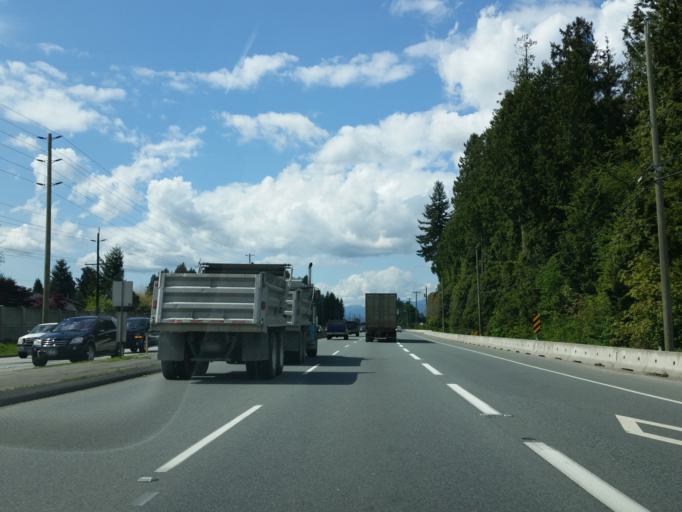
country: CA
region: British Columbia
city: Pitt Meadows
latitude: 49.2265
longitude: -122.6775
